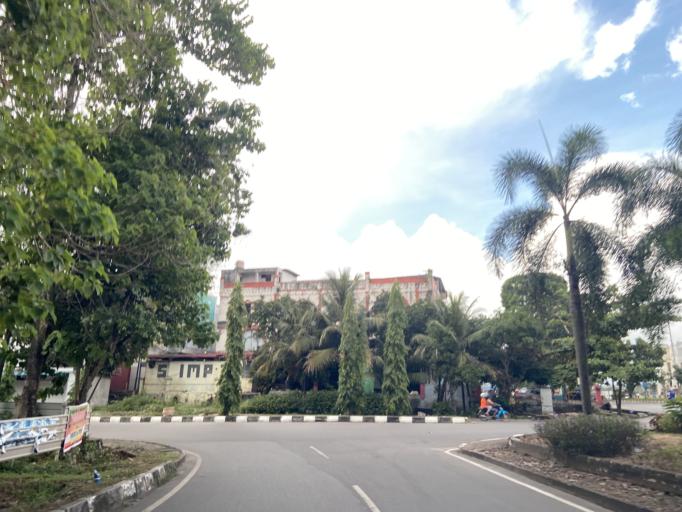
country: SG
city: Singapore
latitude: 1.1486
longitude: 104.0035
